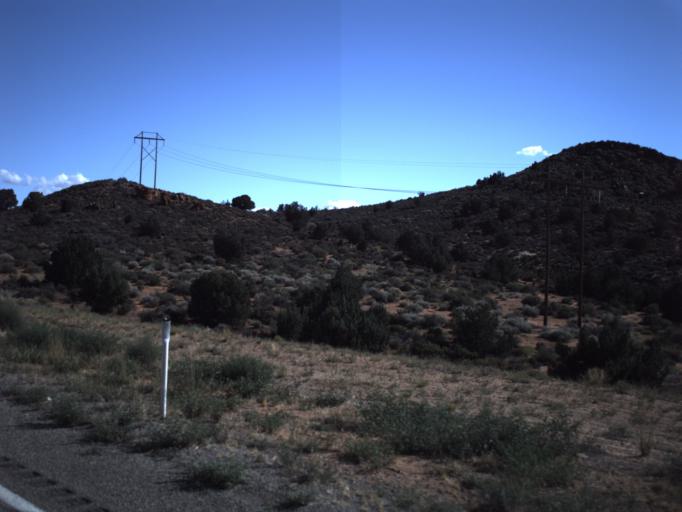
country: US
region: Utah
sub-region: Washington County
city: Toquerville
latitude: 37.2767
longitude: -113.3035
